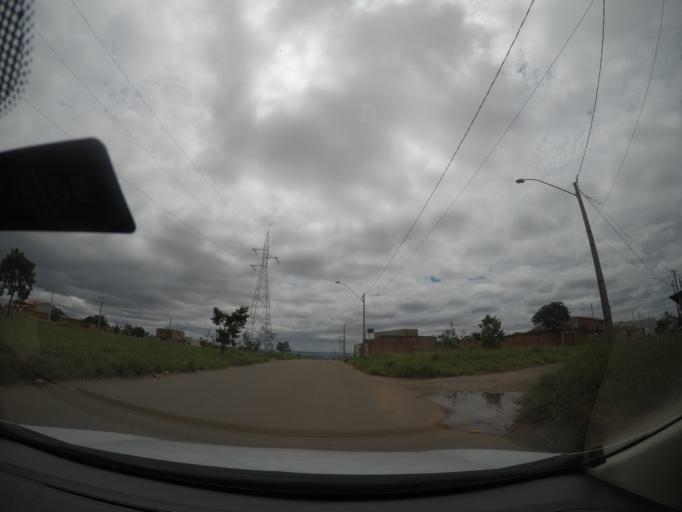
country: BR
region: Goias
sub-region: Trindade
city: Trindade
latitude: -16.7454
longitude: -49.3840
